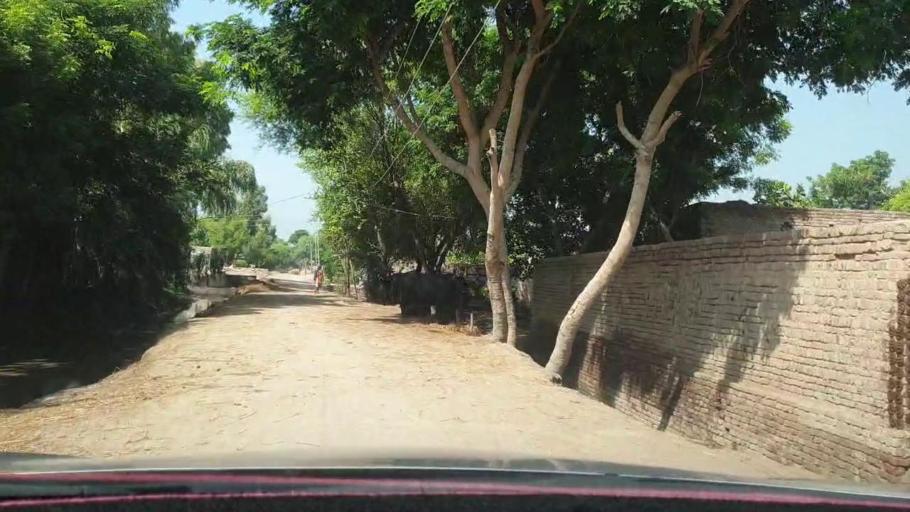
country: PK
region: Sindh
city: Warah
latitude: 27.4555
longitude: 67.8635
